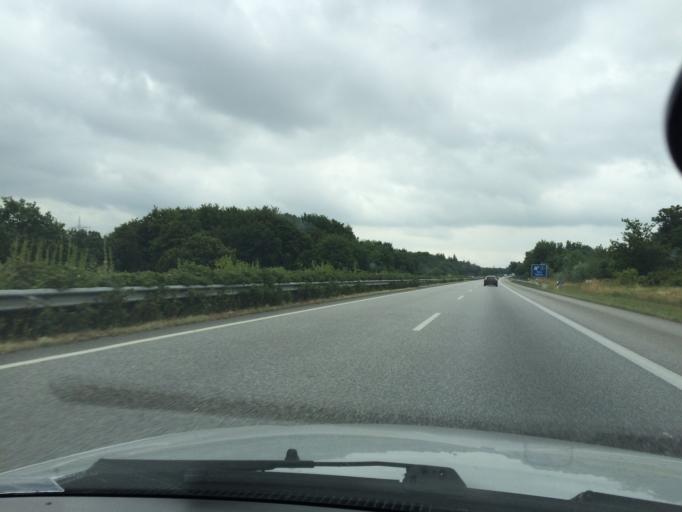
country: DE
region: Schleswig-Holstein
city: Tarp
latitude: 54.6758
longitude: 9.4226
